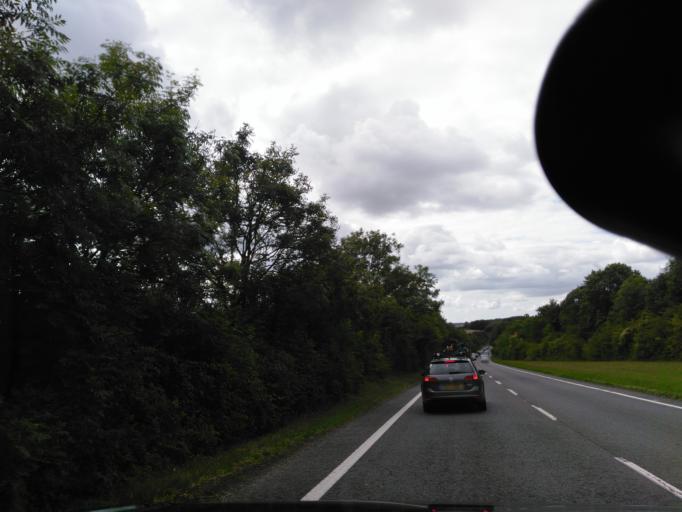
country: GB
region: England
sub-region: Dorset
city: Blandford Forum
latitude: 50.8663
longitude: -2.1464
